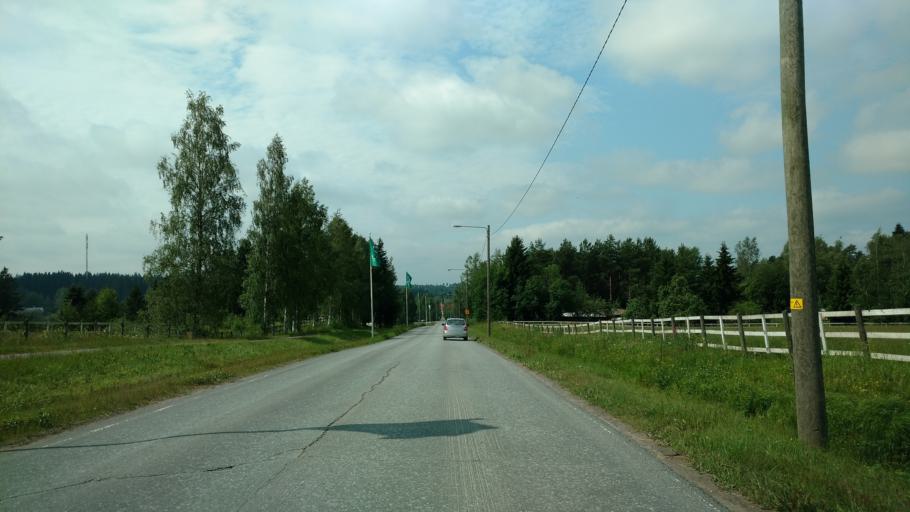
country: FI
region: Haeme
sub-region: Forssa
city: Ypaejae
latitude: 60.8045
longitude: 23.2917
